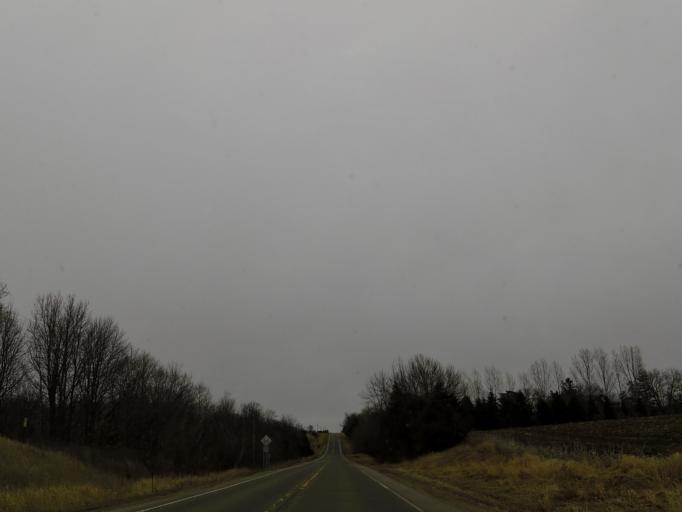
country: US
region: Minnesota
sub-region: Le Sueur County
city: Le Sueur
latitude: 44.5431
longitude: -93.8824
